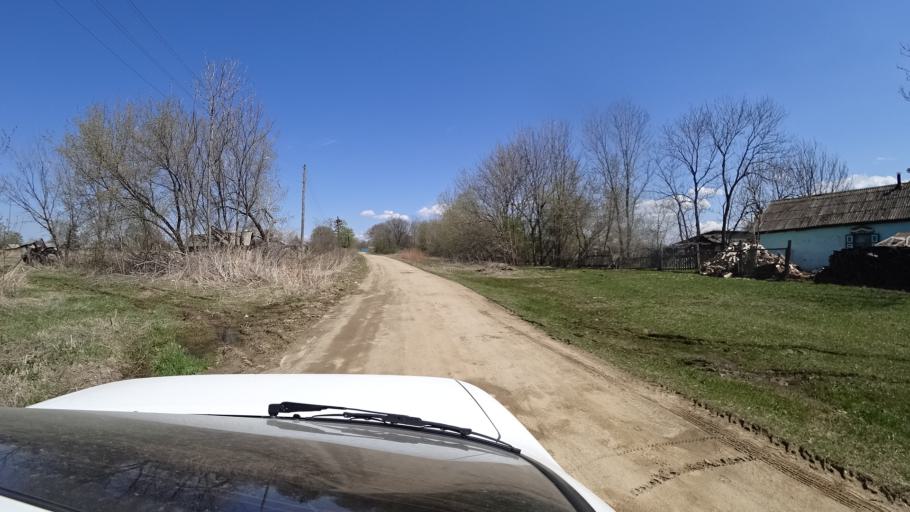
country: RU
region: Primorskiy
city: Dal'nerechensk
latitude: 45.7945
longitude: 133.7689
